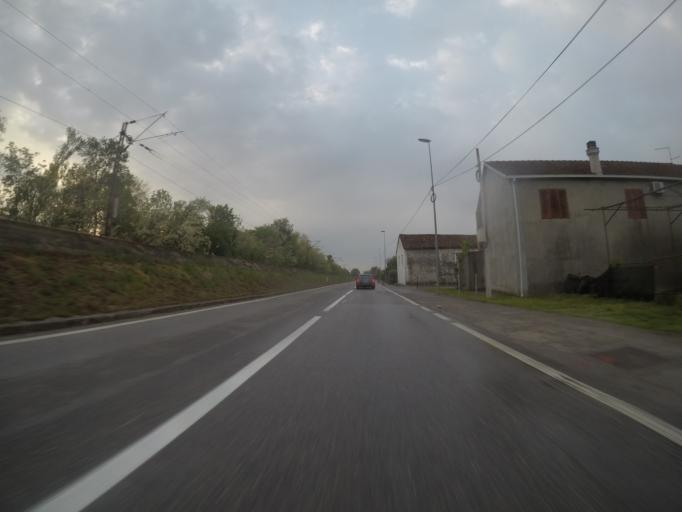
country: ME
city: Mojanovici
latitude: 42.3053
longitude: 19.1876
